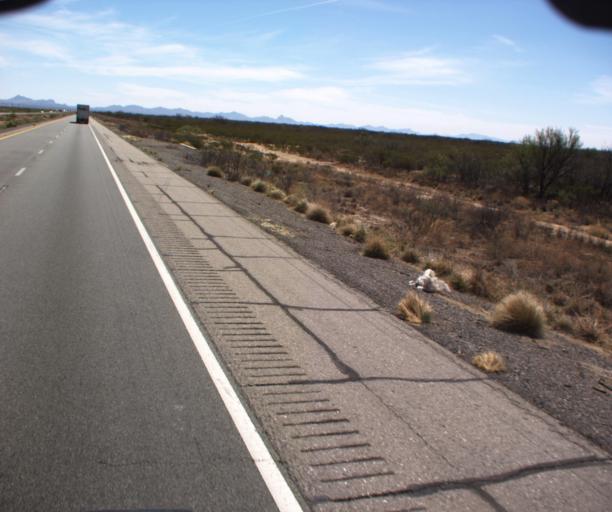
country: US
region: Arizona
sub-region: Cochise County
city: Willcox
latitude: 32.2909
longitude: -109.3266
